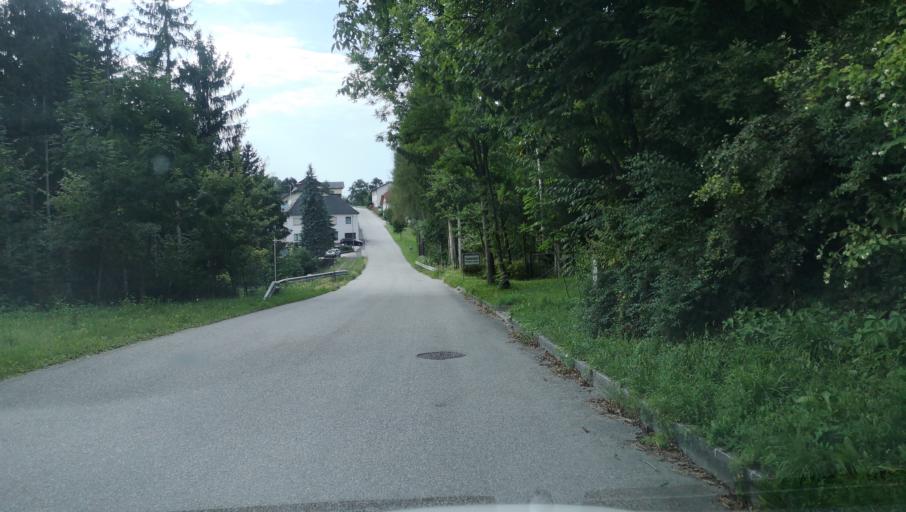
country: AT
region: Lower Austria
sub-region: Politischer Bezirk Amstetten
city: Zeillern
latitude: 48.1569
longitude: 14.8241
